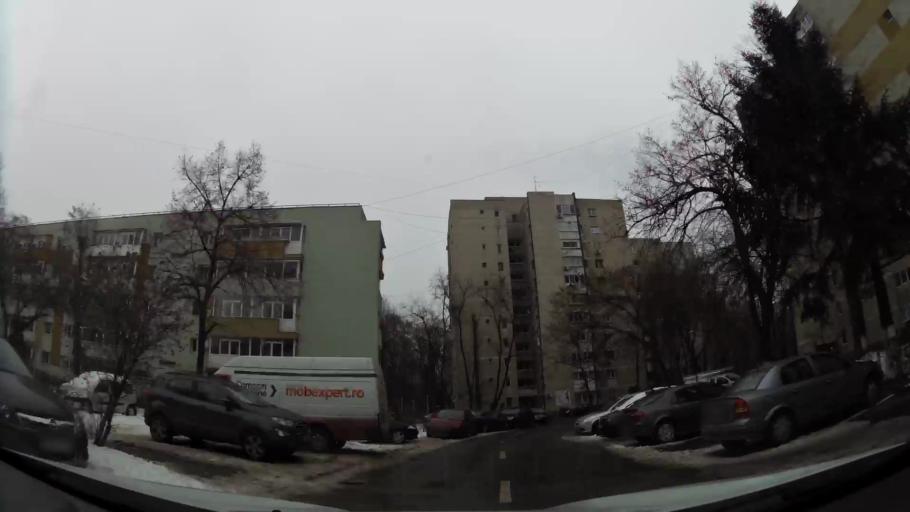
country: RO
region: Ilfov
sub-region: Comuna Chiajna
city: Rosu
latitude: 44.4255
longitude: 26.0281
